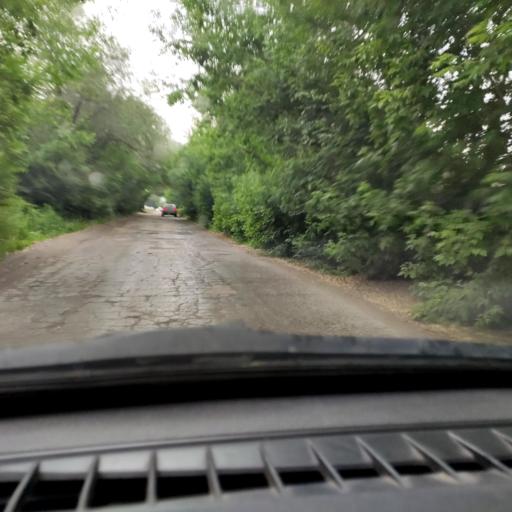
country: RU
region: Samara
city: Tol'yatti
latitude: 53.5212
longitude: 49.4545
